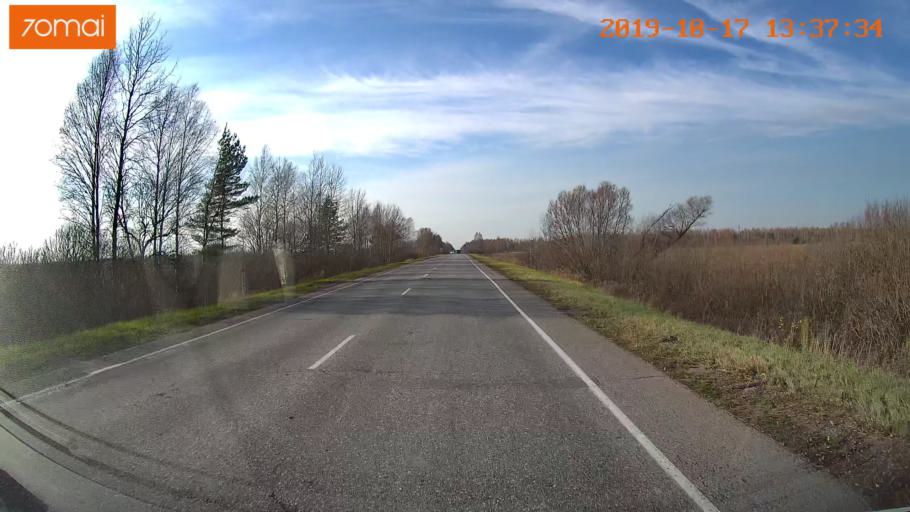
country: RU
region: Rjazan
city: Tuma
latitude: 55.1420
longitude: 40.6355
